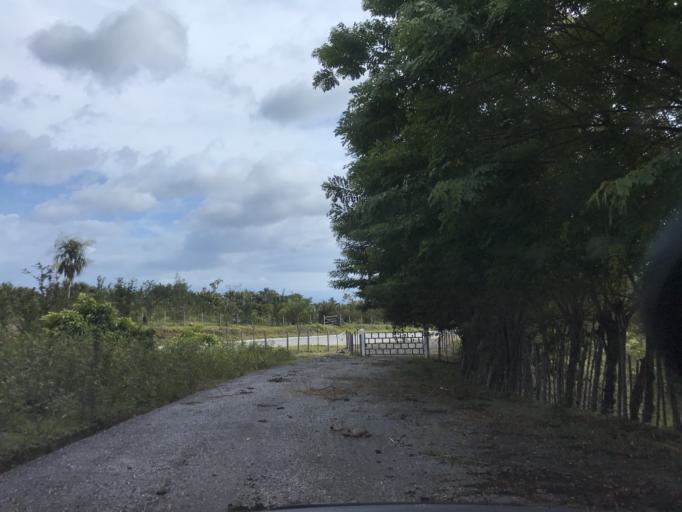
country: GT
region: Izabal
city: Morales
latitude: 15.6251
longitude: -89.0603
